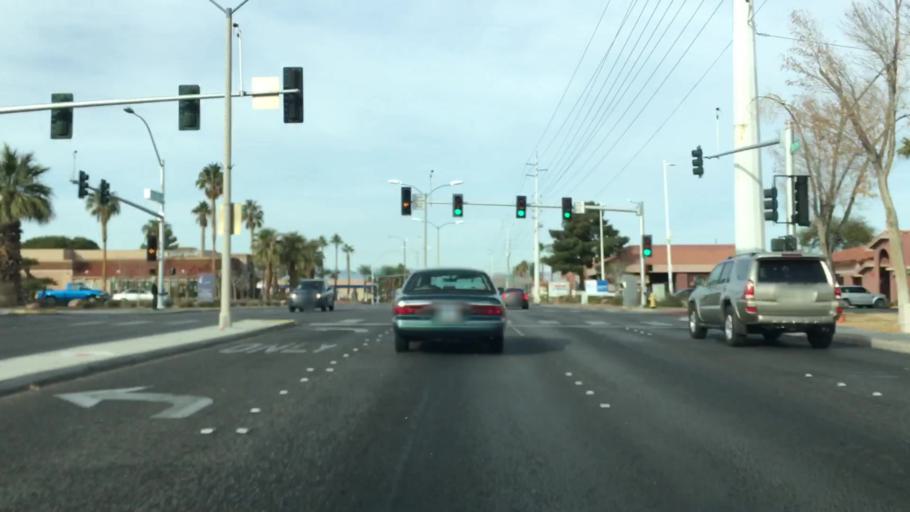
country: US
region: Nevada
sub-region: Clark County
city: Whitney
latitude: 36.0689
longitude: -115.0824
